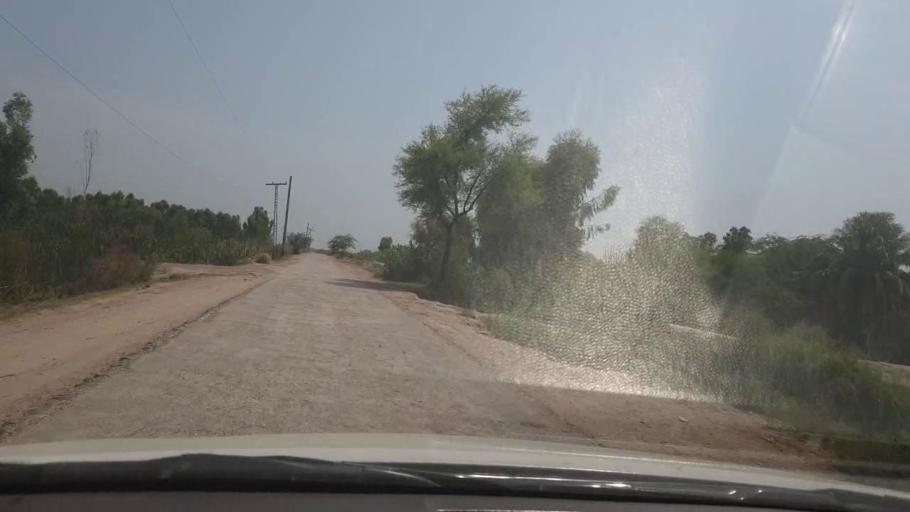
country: PK
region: Sindh
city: Garhi Yasin
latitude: 27.9702
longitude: 68.5038
